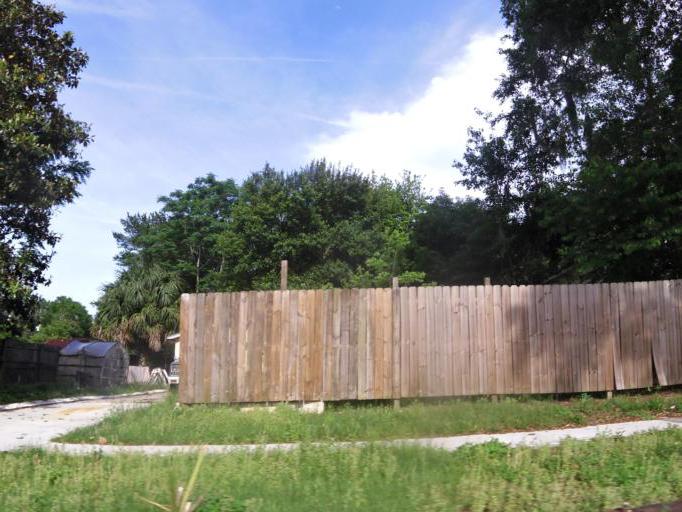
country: US
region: Florida
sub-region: Duval County
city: Jacksonville
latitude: 30.3366
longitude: -81.5922
